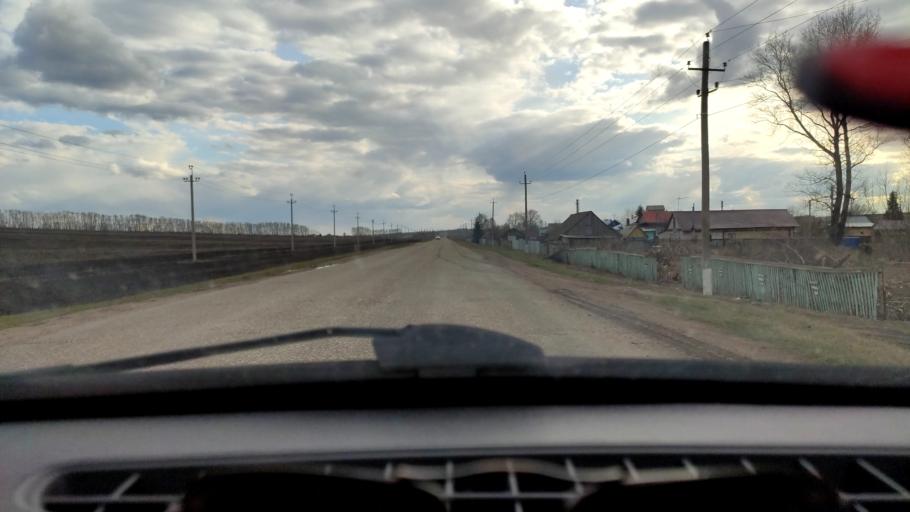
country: RU
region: Bashkortostan
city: Karmaskaly
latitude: 54.3993
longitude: 56.2484
